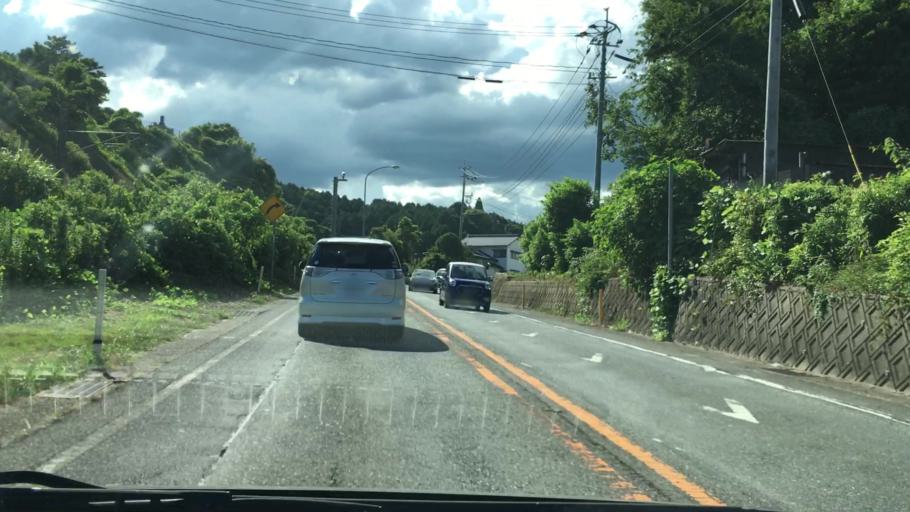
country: JP
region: Saga Prefecture
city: Takeocho-takeo
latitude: 33.1901
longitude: 129.9847
